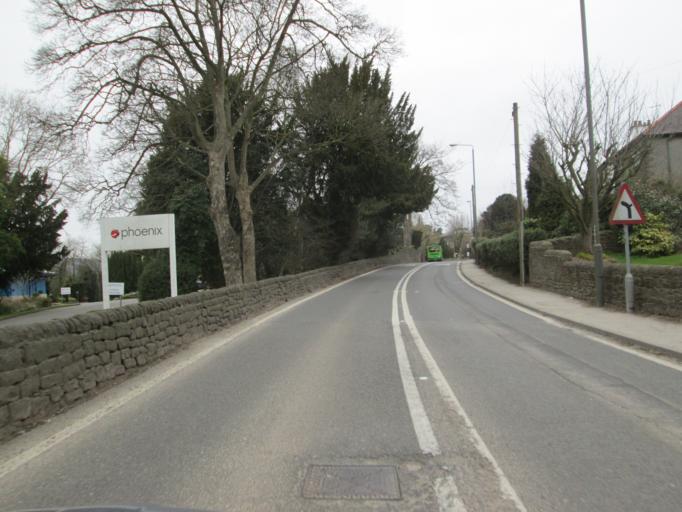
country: GB
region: England
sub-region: Derbyshire
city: Matlock
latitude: 53.1511
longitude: -1.5764
